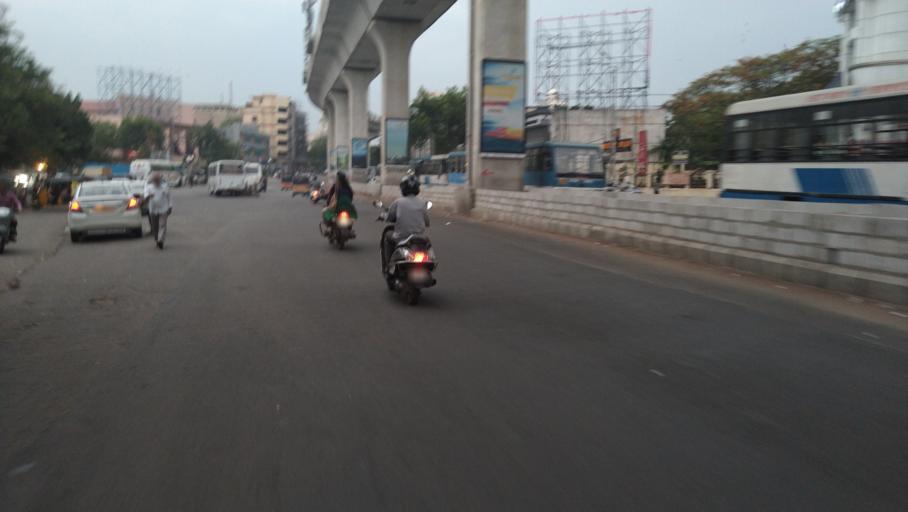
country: IN
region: Telangana
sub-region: Hyderabad
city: Malkajgiri
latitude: 17.4384
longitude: 78.4995
